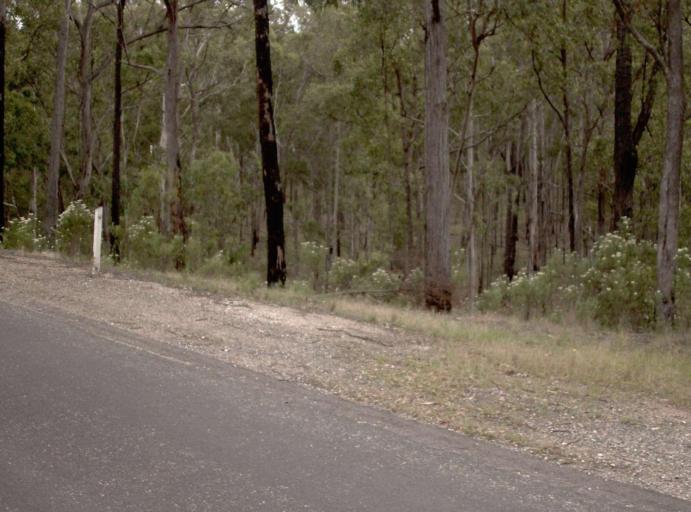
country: AU
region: Victoria
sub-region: East Gippsland
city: Bairnsdale
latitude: -37.7085
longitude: 147.5939
